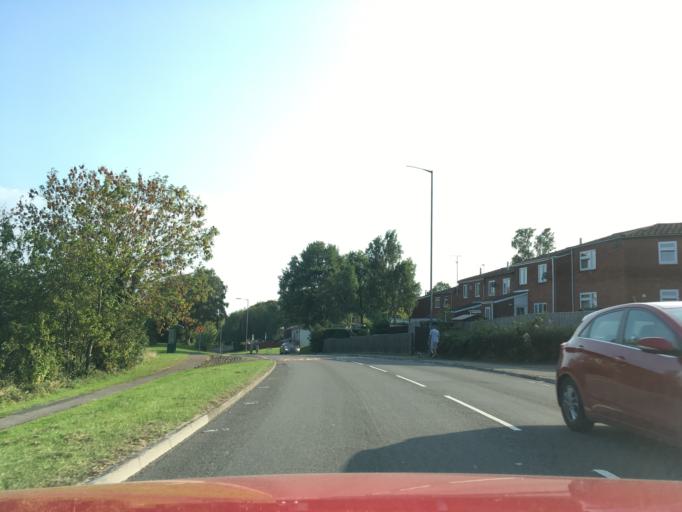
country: GB
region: Wales
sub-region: Torfaen County Borough
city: Cwmbran
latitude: 51.6617
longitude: -3.0461
